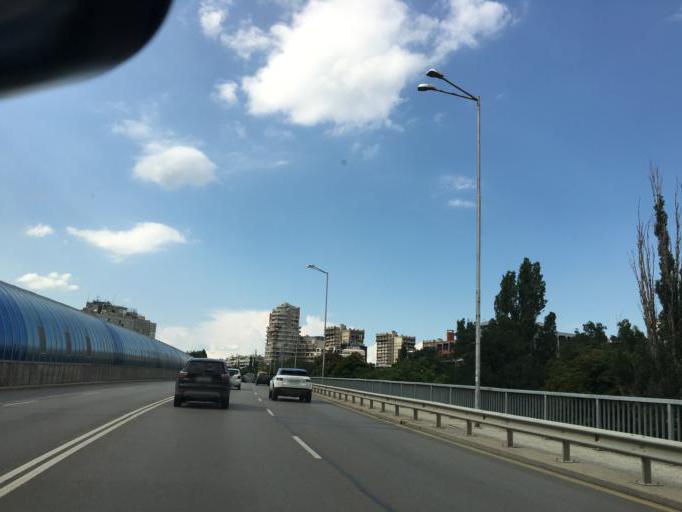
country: BG
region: Sofia-Capital
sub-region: Stolichna Obshtina
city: Sofia
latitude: 42.6672
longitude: 23.3533
